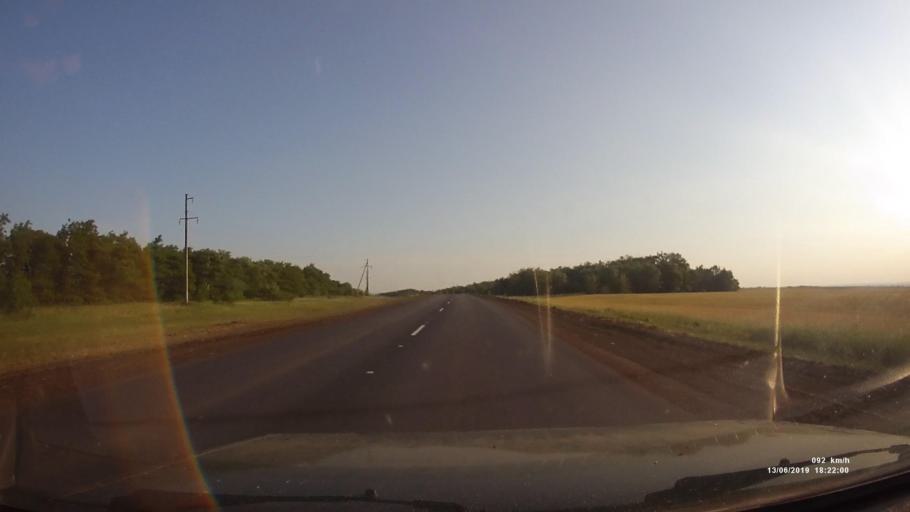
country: RU
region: Rostov
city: Kazanskaya
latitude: 49.8640
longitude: 41.2832
